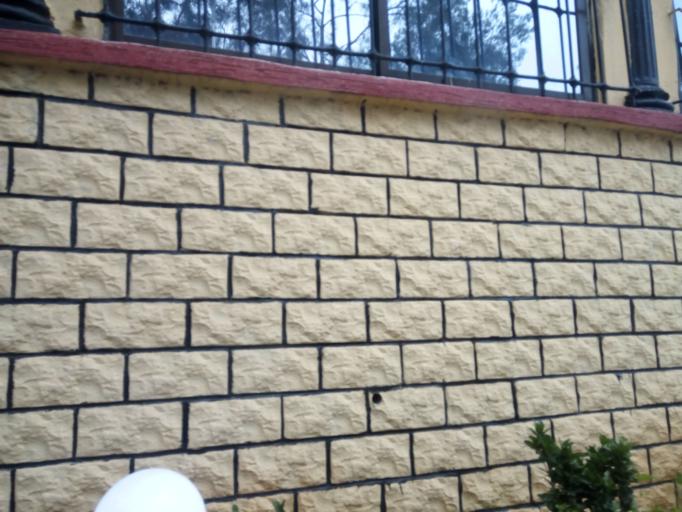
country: DZ
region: Tipaza
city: Tipasa
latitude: 36.5752
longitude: 2.5544
